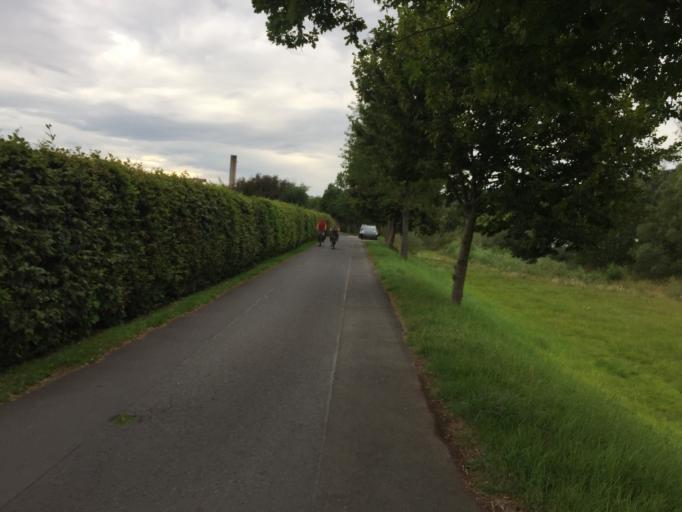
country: DE
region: Hesse
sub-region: Regierungsbezirk Kassel
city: Rotenburg an der Fulda
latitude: 50.9916
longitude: 9.7454
